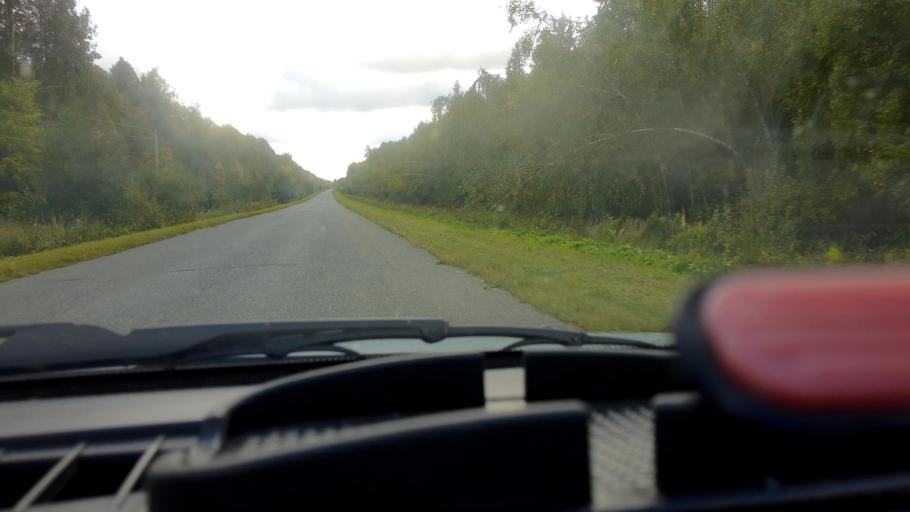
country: RU
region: Mariy-El
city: Kilemary
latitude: 56.9188
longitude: 46.7184
